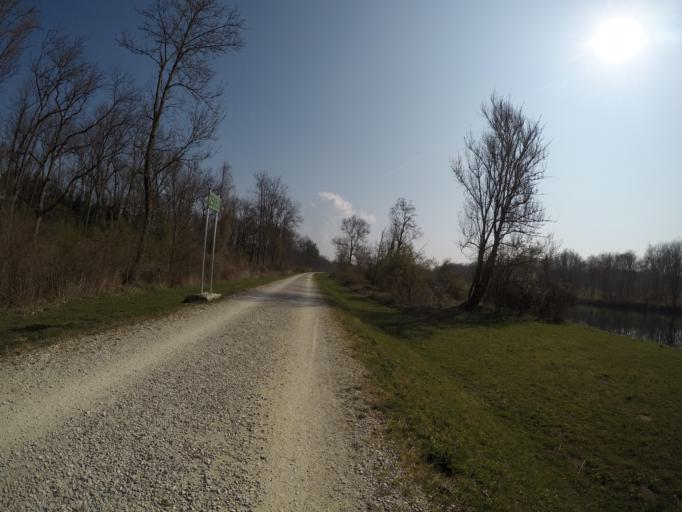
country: DE
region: Bavaria
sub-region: Swabia
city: Leipheim
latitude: 48.4588
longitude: 10.2350
